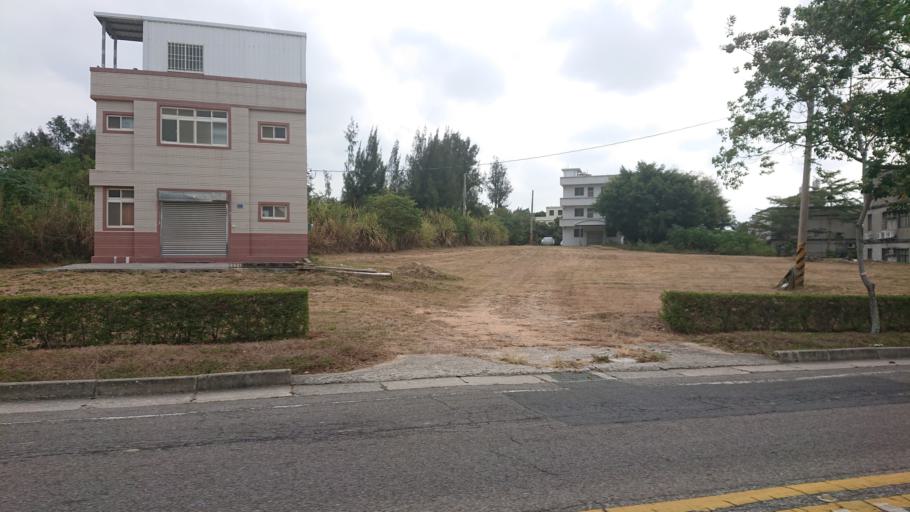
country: TW
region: Fukien
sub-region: Kinmen
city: Jincheng
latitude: 24.4212
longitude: 118.3174
